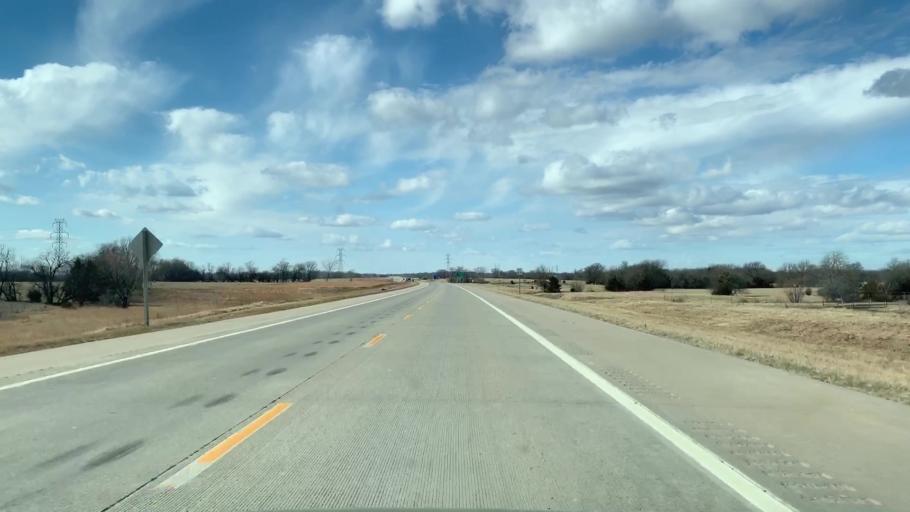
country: US
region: Kansas
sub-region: Labette County
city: Parsons
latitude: 37.3626
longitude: -95.2339
